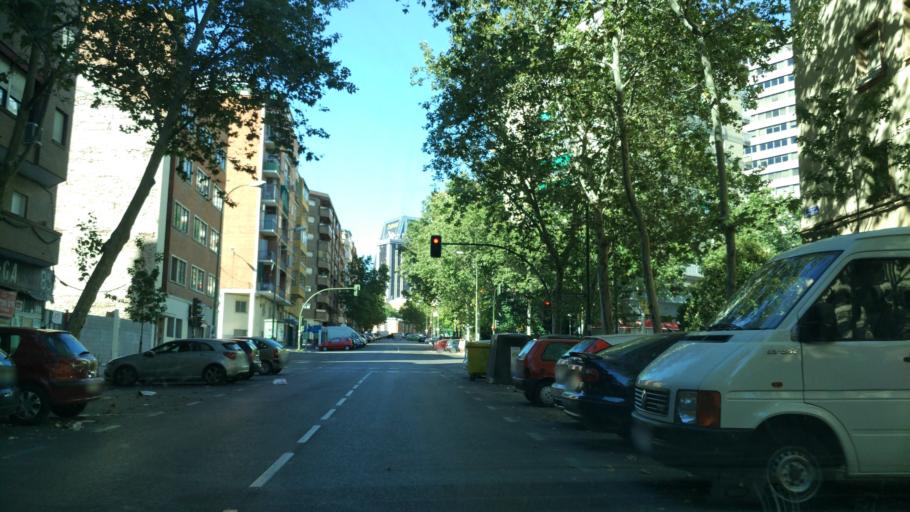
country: ES
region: Madrid
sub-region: Provincia de Madrid
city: Chamartin
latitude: 40.4621
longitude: -3.6949
